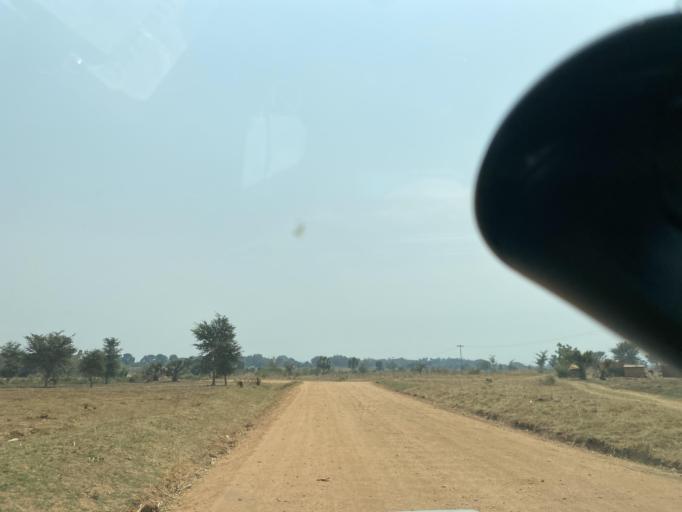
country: ZM
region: Lusaka
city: Kafue
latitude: -15.6312
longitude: 28.0990
